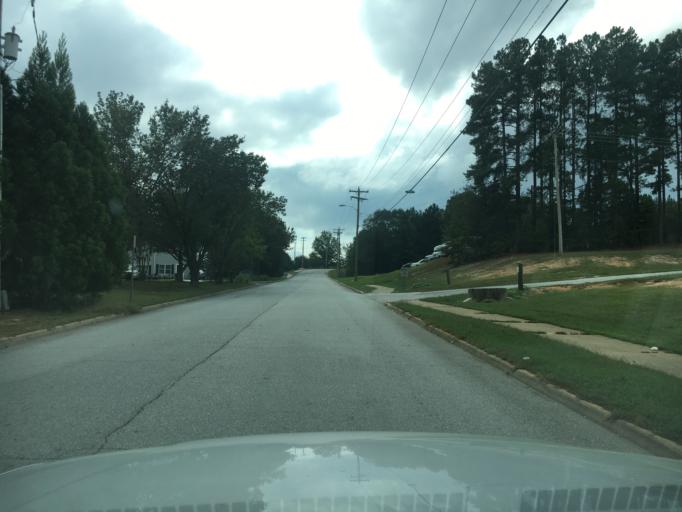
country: US
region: South Carolina
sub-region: Greenville County
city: Greer
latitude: 34.9531
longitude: -82.2337
